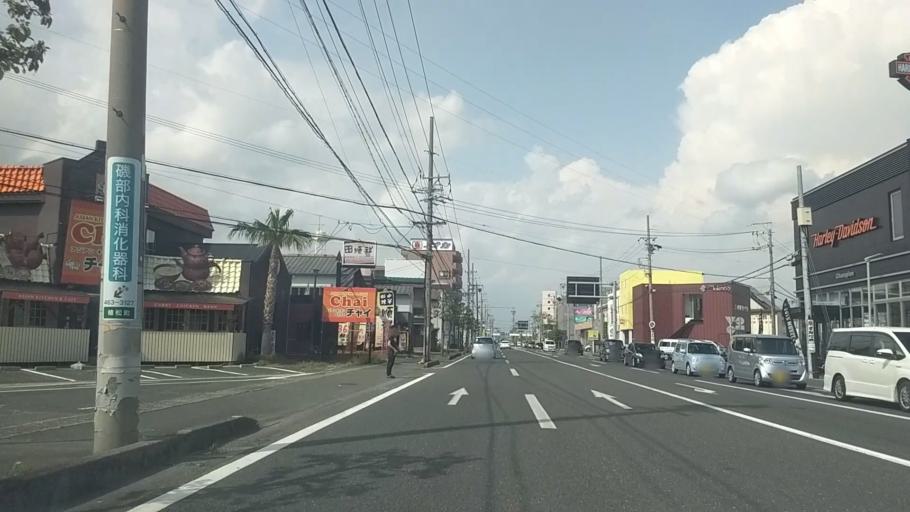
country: JP
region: Shizuoka
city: Hamamatsu
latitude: 34.7137
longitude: 137.7602
